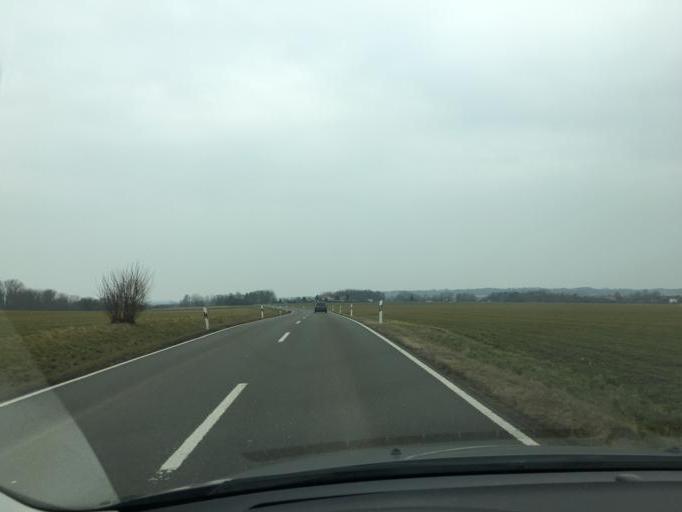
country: DE
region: Thuringia
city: Gerstenberg
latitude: 51.0256
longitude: 12.4520
